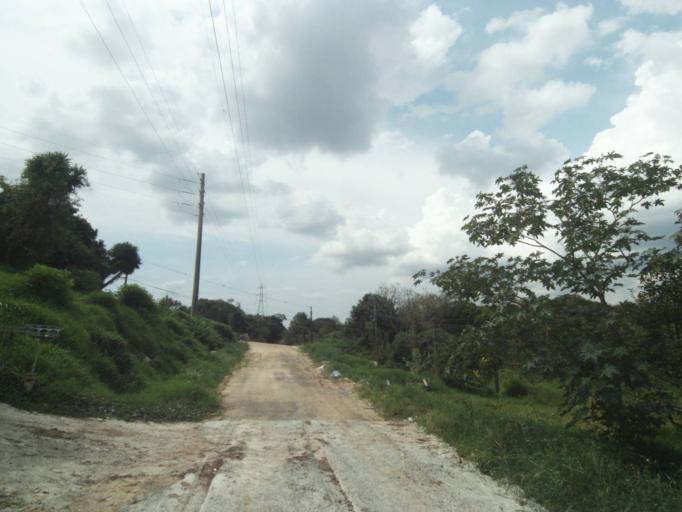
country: BR
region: Parana
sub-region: Pinhais
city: Pinhais
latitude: -25.4007
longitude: -49.1946
